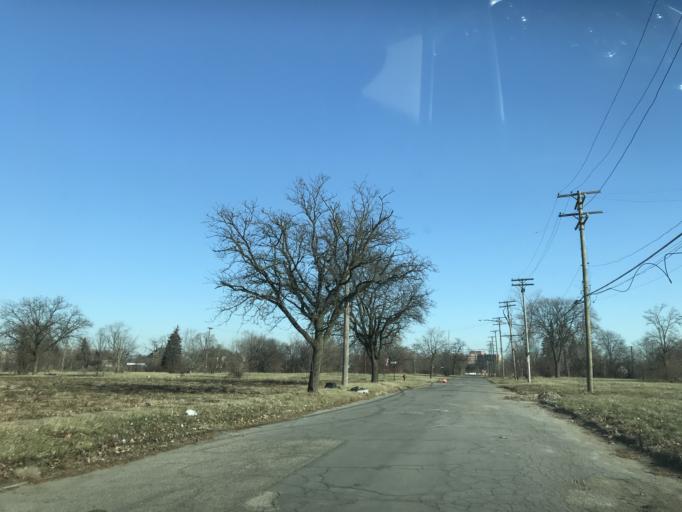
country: US
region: Michigan
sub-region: Wayne County
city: Dearborn
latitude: 42.3417
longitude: -83.1193
